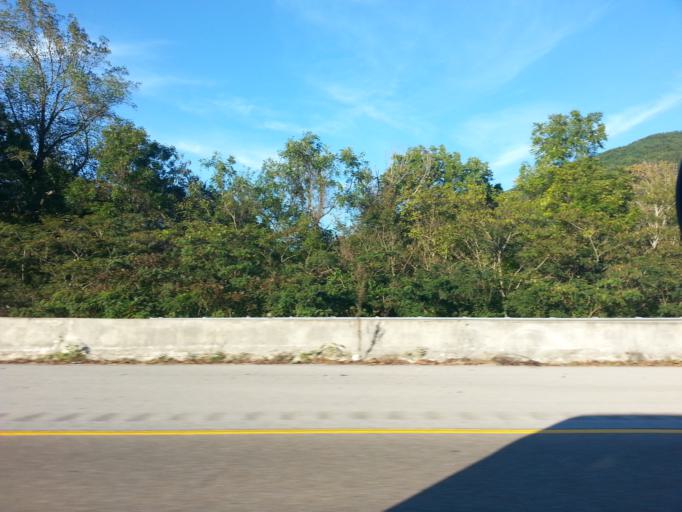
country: US
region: Tennessee
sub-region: Blount County
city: Wildwood
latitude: 35.7377
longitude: -83.8264
